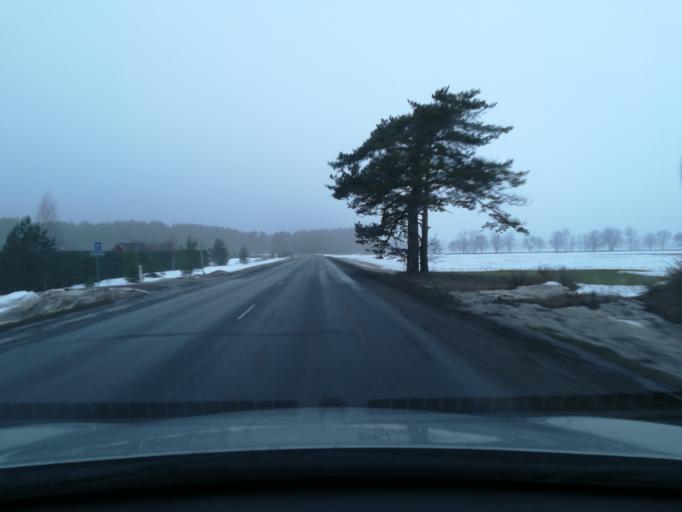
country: EE
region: Harju
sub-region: Raasiku vald
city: Arukula
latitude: 59.3537
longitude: 25.0803
